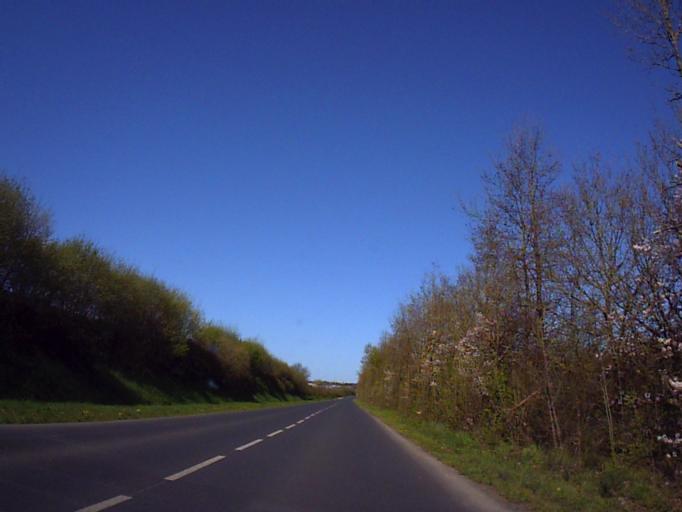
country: FR
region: Brittany
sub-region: Departement des Cotes-d'Armor
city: Caulnes
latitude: 48.2723
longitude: -2.1761
